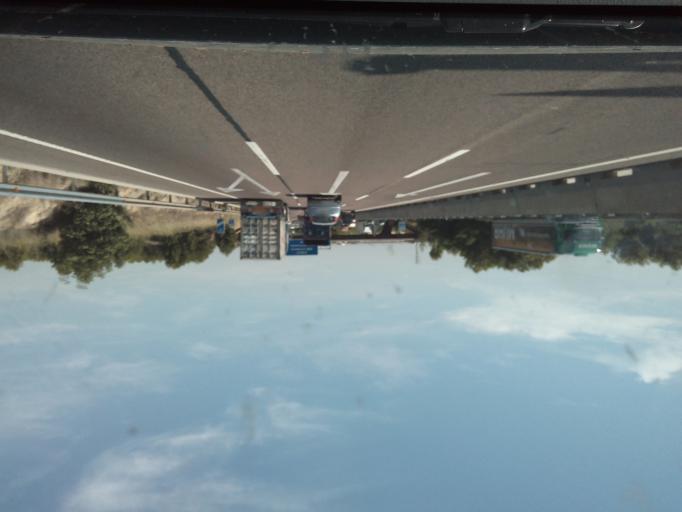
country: ES
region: Valencia
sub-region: Provincia de Valencia
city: Manises
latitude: 39.5277
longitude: -0.4661
